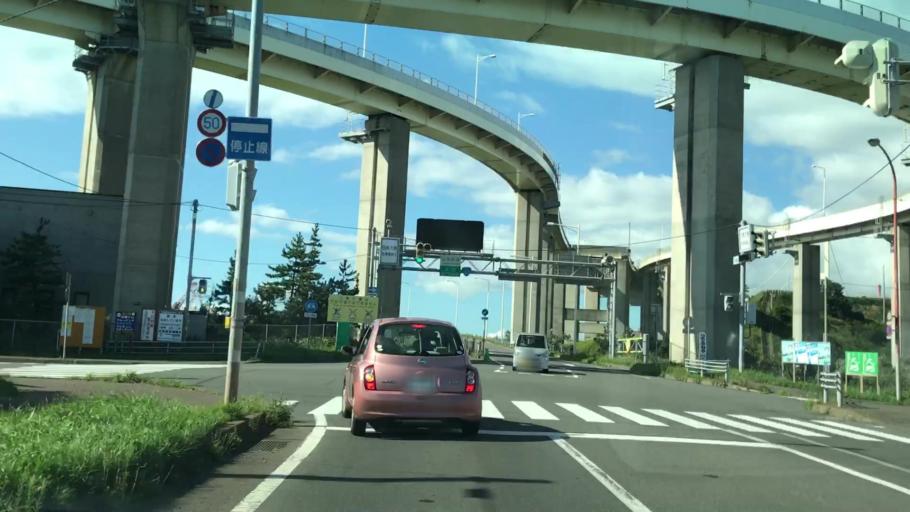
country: JP
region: Hokkaido
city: Muroran
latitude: 42.3417
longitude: 140.9500
